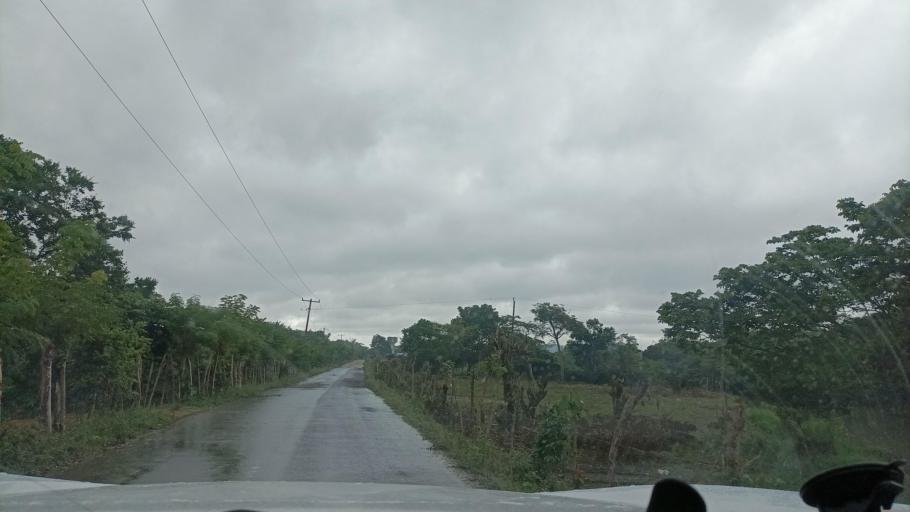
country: MX
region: Veracruz
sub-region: Moloacan
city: Cuichapa
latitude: 17.7584
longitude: -94.3941
